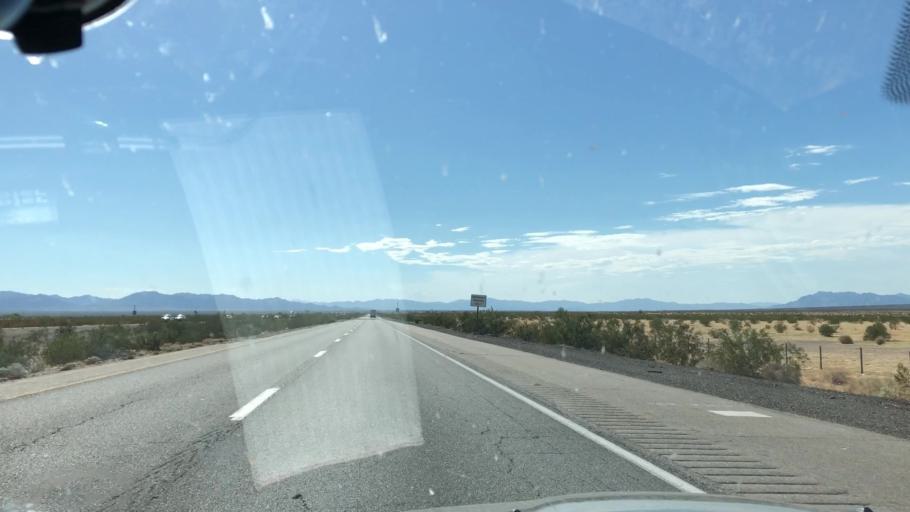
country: US
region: California
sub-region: Riverside County
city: Mesa Verde
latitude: 33.6254
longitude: -115.0525
